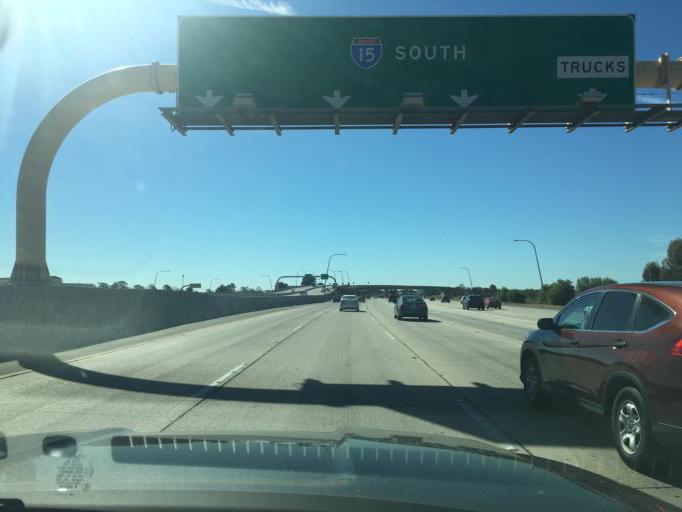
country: US
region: California
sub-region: San Diego County
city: Poway
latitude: 32.8663
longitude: -117.1092
